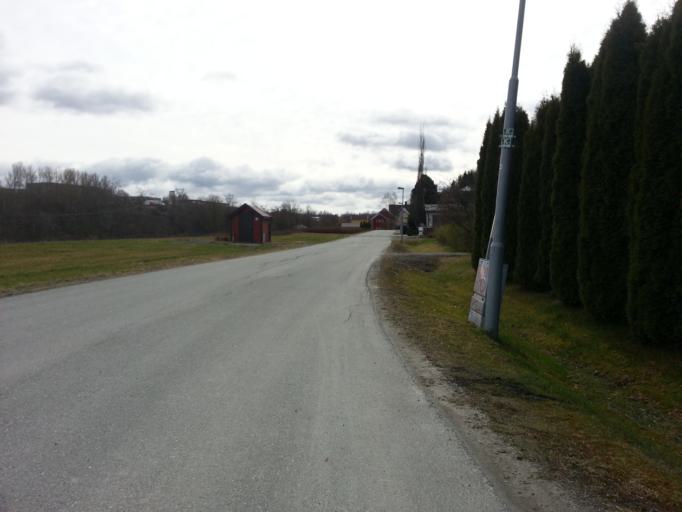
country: NO
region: Sor-Trondelag
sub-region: Trondheim
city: Trondheim
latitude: 63.4057
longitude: 10.3875
